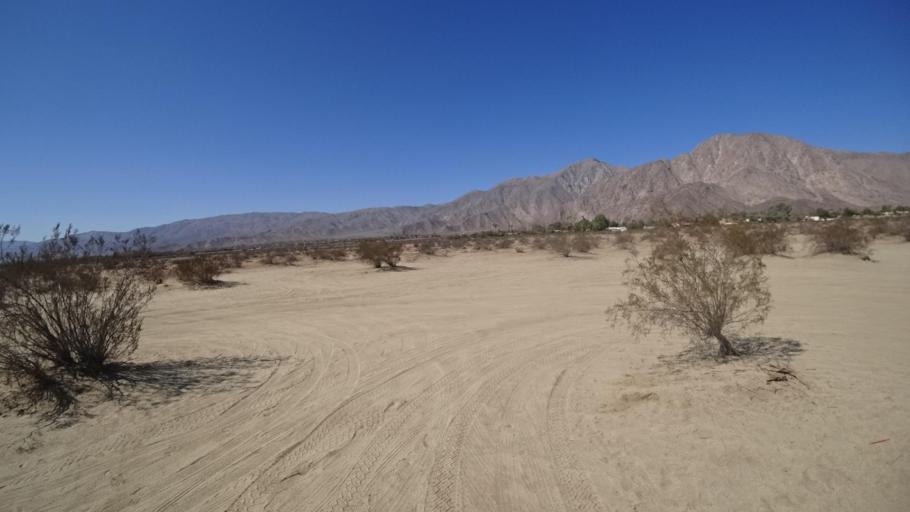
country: US
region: California
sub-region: San Diego County
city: Borrego Springs
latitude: 33.2899
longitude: -116.3770
